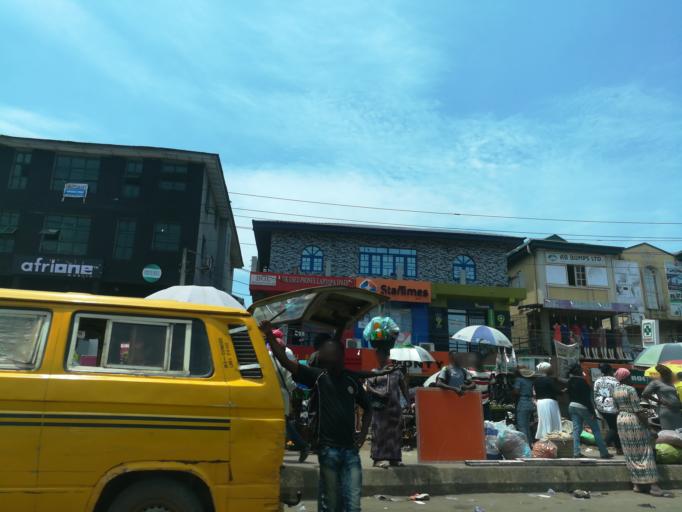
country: NG
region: Lagos
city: Ikorodu
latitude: 6.6222
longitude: 3.4993
